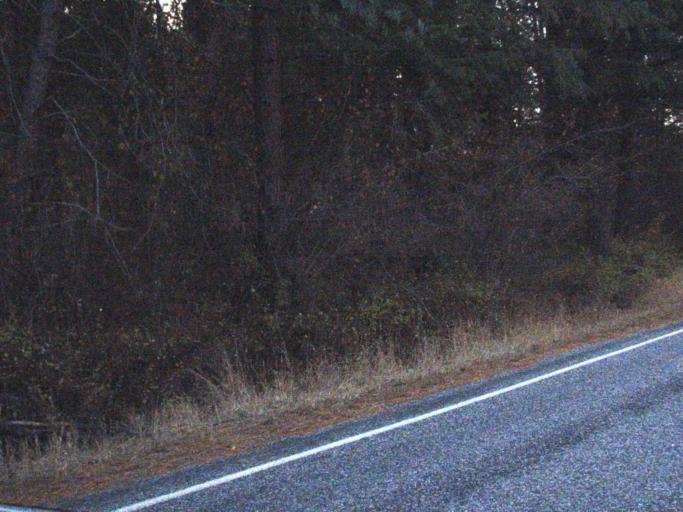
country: US
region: Washington
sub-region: Ferry County
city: Republic
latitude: 48.2974
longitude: -118.7342
